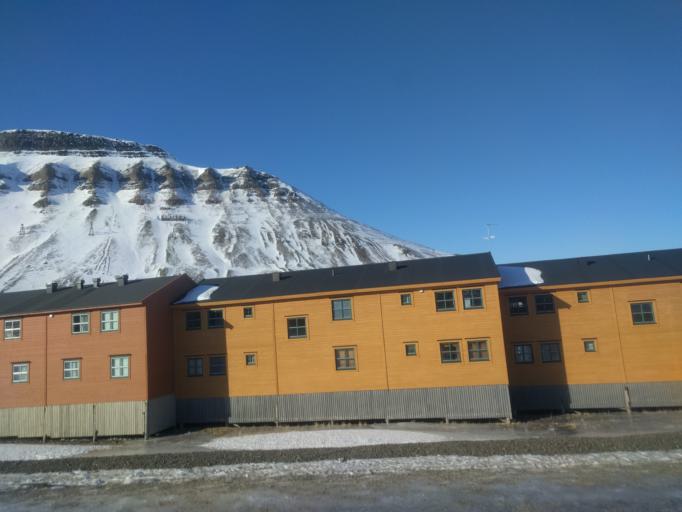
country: SJ
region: Svalbard
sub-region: Spitsbergen
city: Longyearbyen
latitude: 78.2149
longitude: 15.6290
